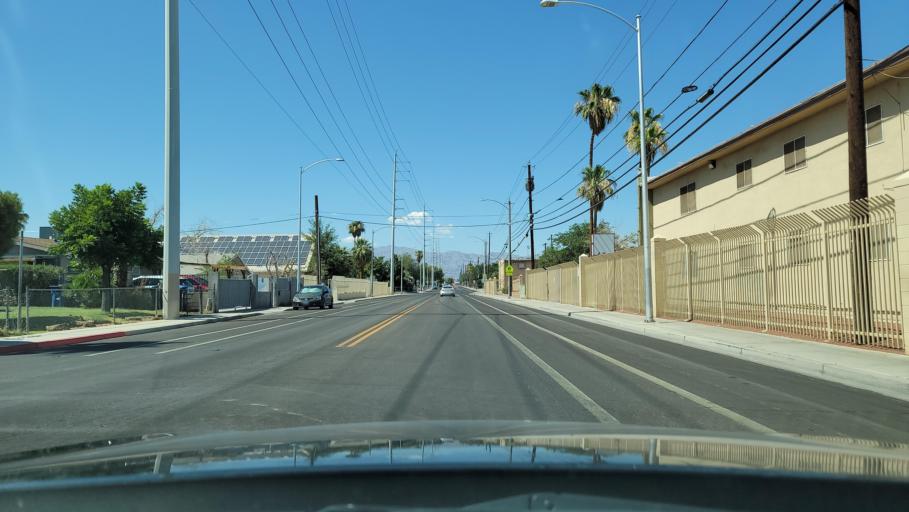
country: US
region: Nevada
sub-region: Clark County
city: Las Vegas
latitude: 36.1906
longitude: -115.1563
